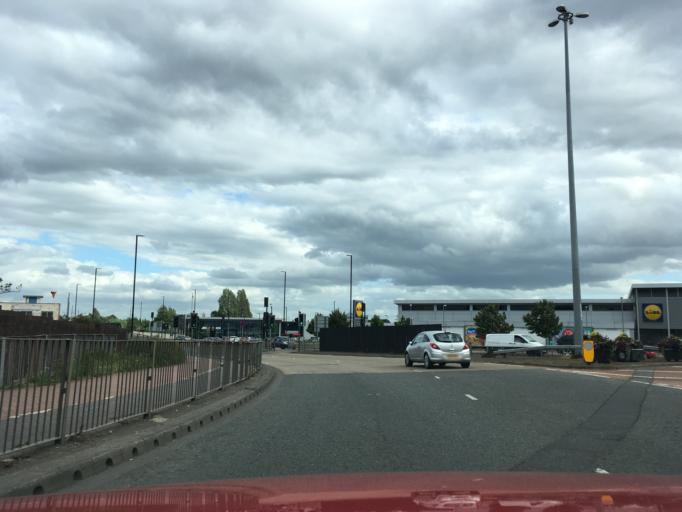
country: GB
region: England
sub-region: Warwickshire
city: Exhall
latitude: 52.4359
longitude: -1.4936
